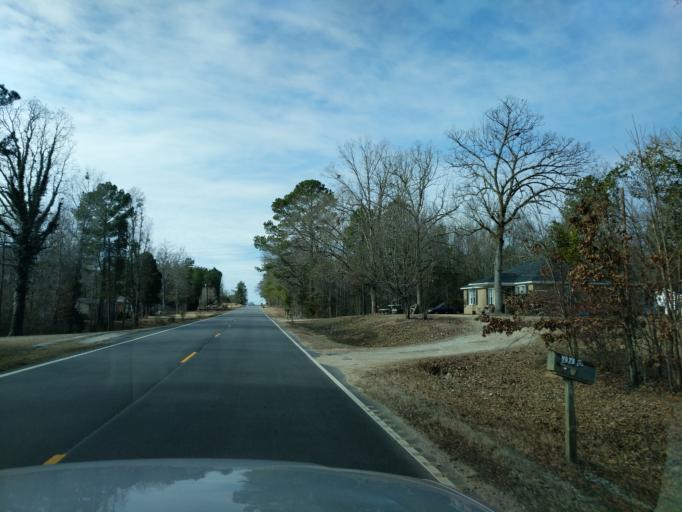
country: US
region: South Carolina
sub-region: Edgefield County
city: Edgefield
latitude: 33.9375
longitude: -81.9452
